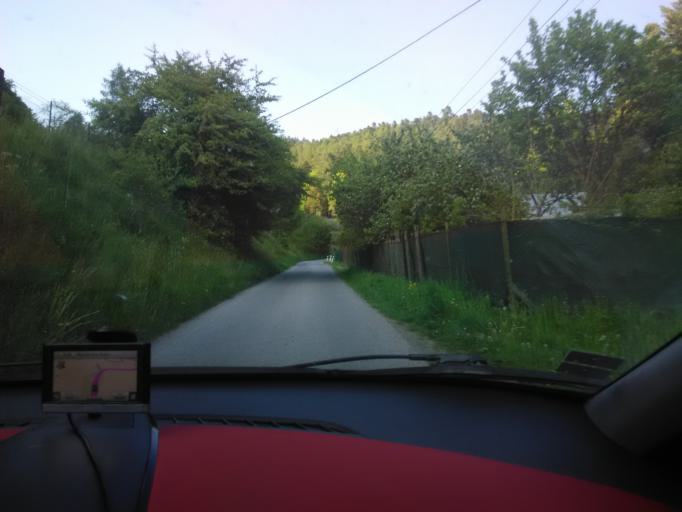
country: SK
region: Presovsky
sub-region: Okres Presov
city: Levoca
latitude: 49.0422
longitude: 20.6029
